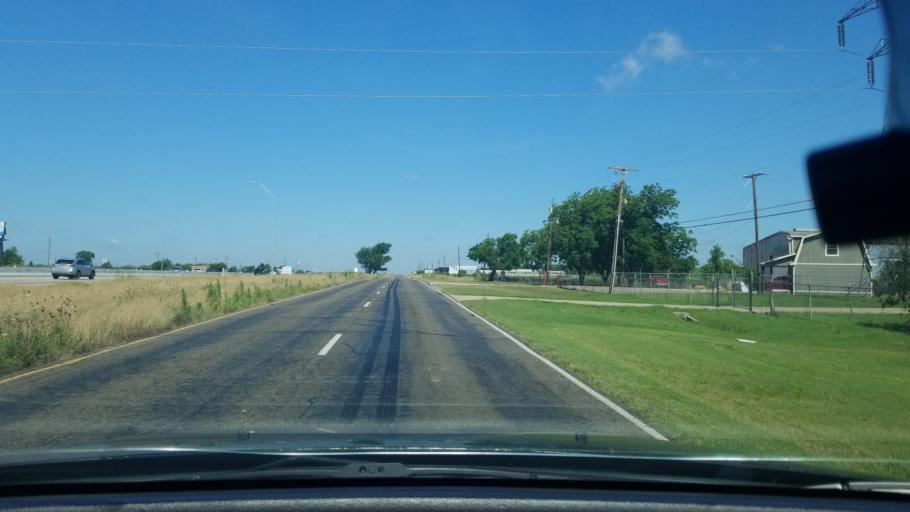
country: US
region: Texas
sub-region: Dallas County
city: Sunnyvale
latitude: 32.7870
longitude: -96.5724
